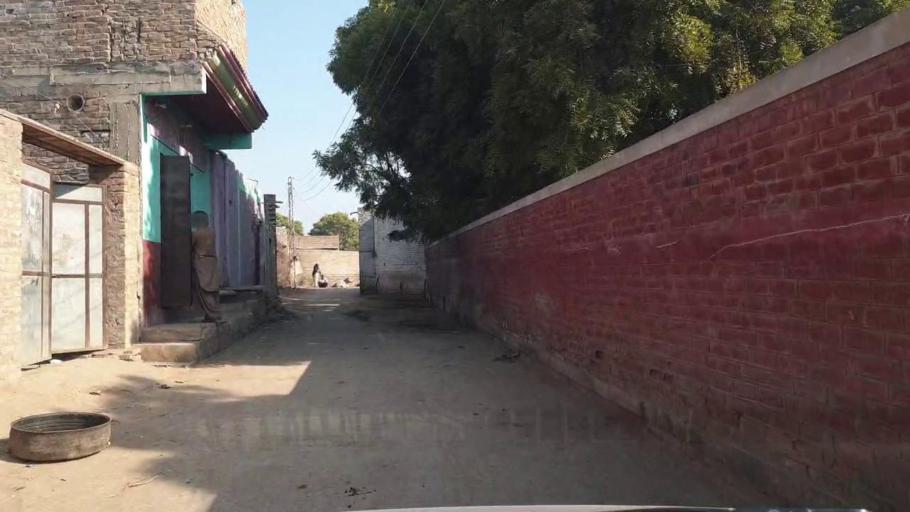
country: PK
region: Sindh
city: Tando Allahyar
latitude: 25.4268
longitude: 68.7568
